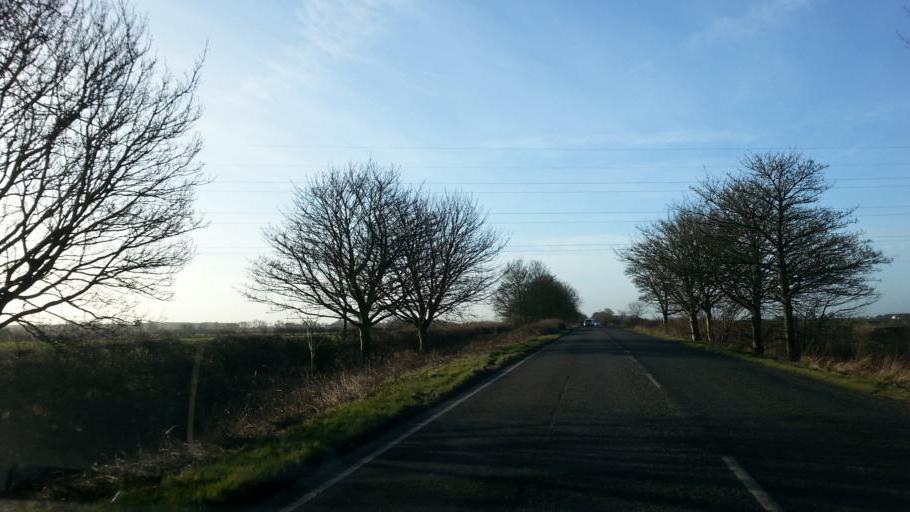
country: GB
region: England
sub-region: Lincolnshire
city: Grantham
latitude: 52.9255
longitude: -0.5728
